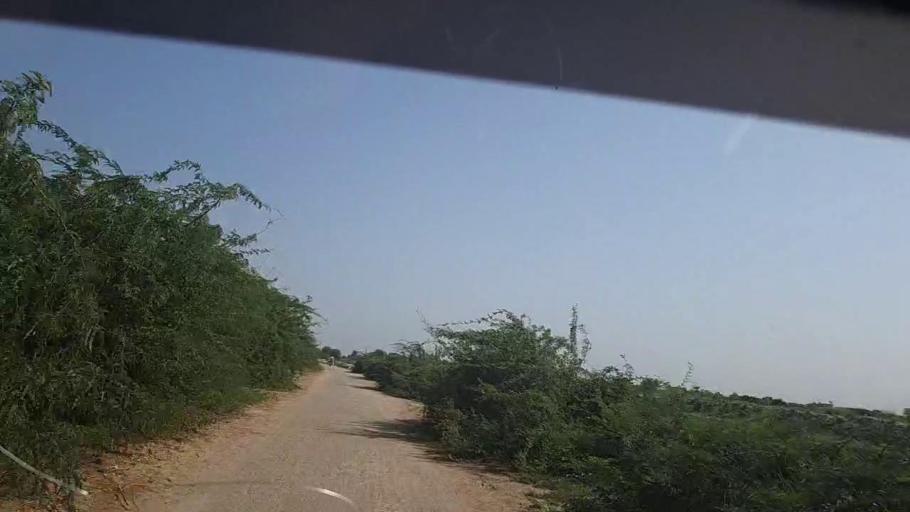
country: PK
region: Sindh
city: Rajo Khanani
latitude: 24.9712
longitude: 68.8710
